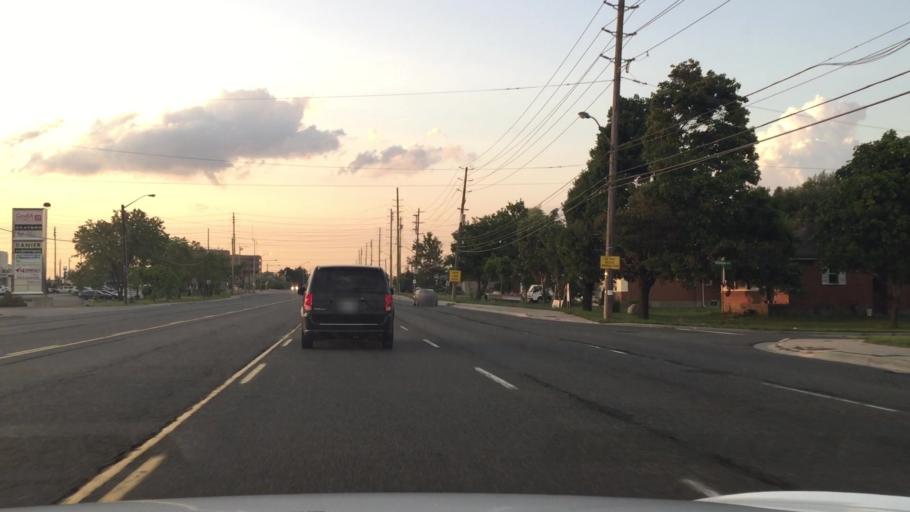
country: CA
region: Ontario
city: Concord
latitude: 43.7975
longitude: -79.4987
